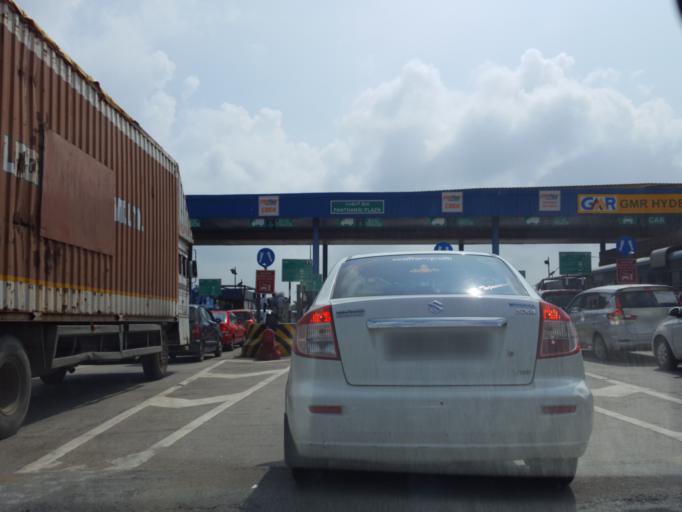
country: IN
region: Telangana
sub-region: Nalgonda
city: Bhongir
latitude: 17.2332
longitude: 78.9601
